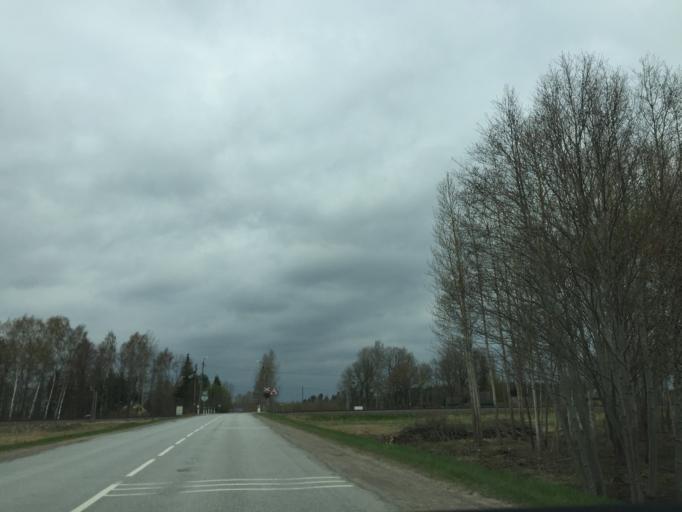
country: EE
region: Tartu
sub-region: Noo vald
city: Noo
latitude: 58.2791
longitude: 26.5284
